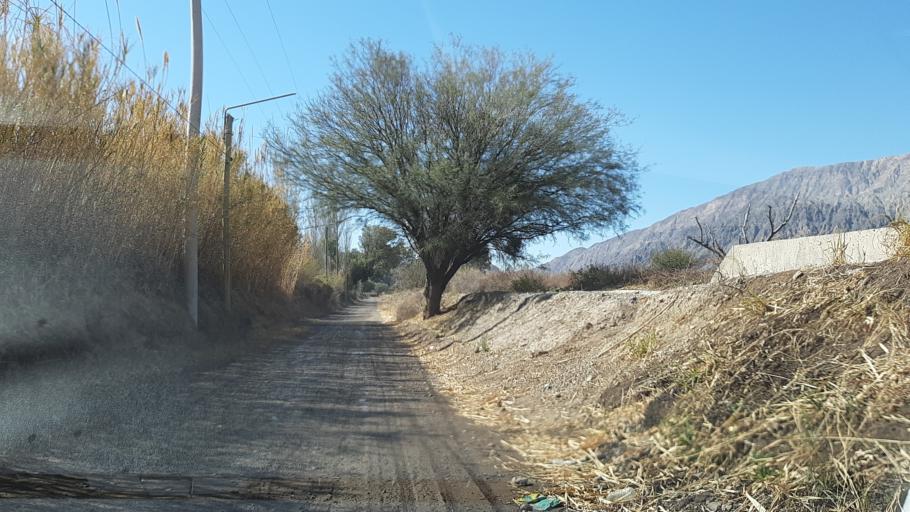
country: AR
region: San Juan
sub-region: Departamento de Zonda
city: Zonda
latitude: -31.5702
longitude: -68.7402
